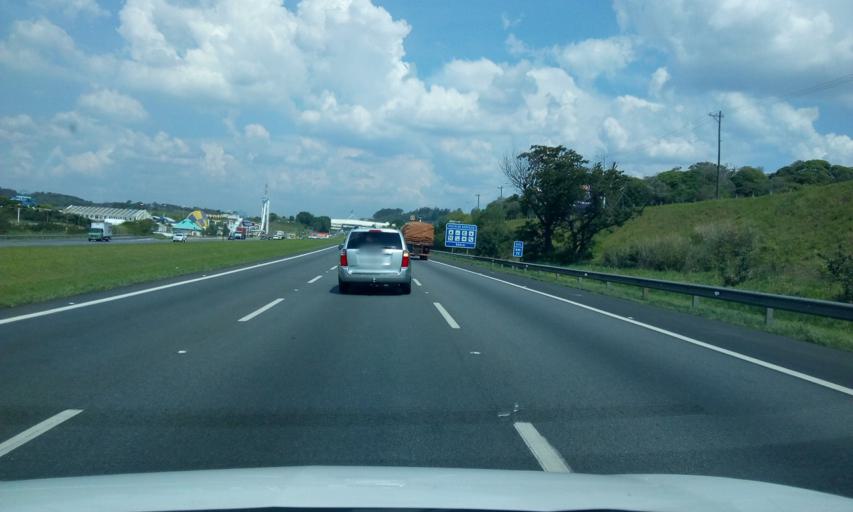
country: BR
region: Sao Paulo
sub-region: Louveira
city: Louveira
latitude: -23.0975
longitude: -47.0154
